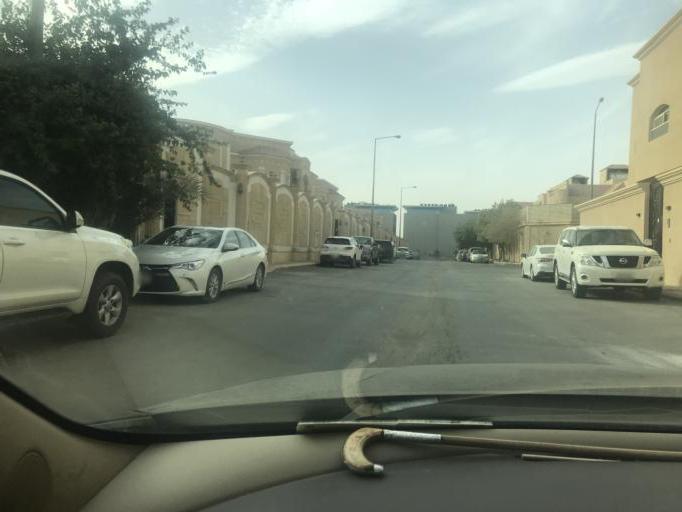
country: SA
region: Ar Riyad
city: Riyadh
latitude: 24.8064
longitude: 46.6683
